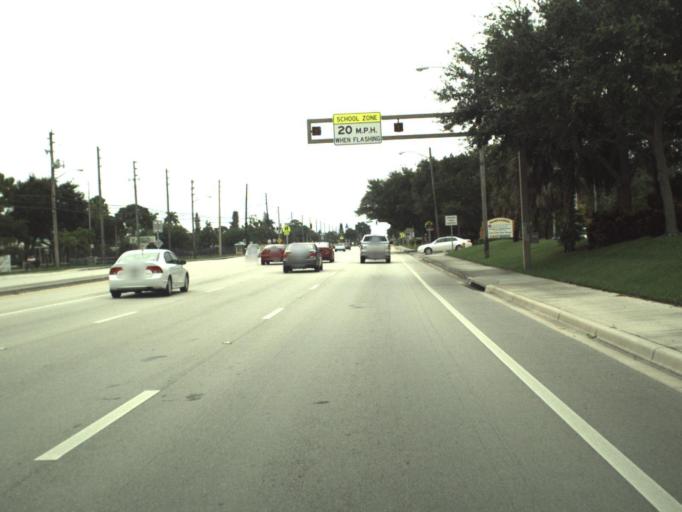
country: US
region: Florida
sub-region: Palm Beach County
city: North Palm Beach
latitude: 26.8004
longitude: -80.1067
